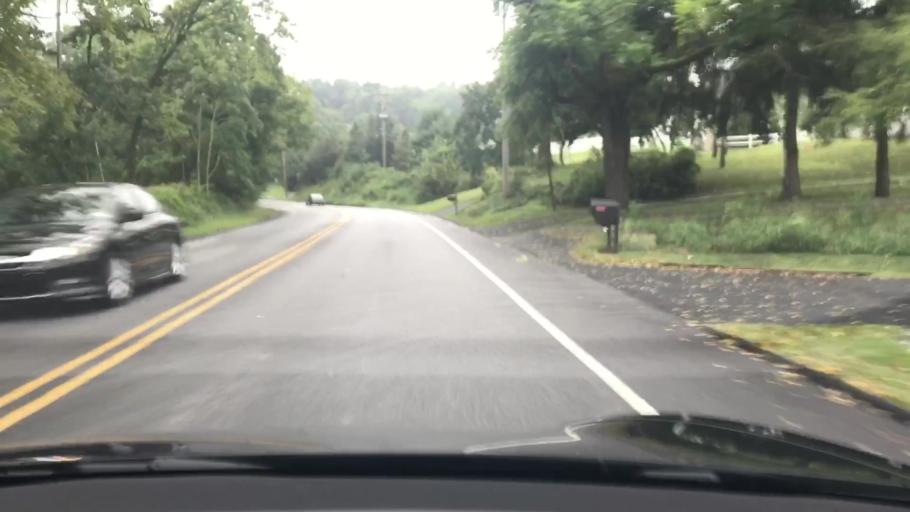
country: US
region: Pennsylvania
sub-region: York County
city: Valley Green
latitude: 40.1661
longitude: -76.8221
